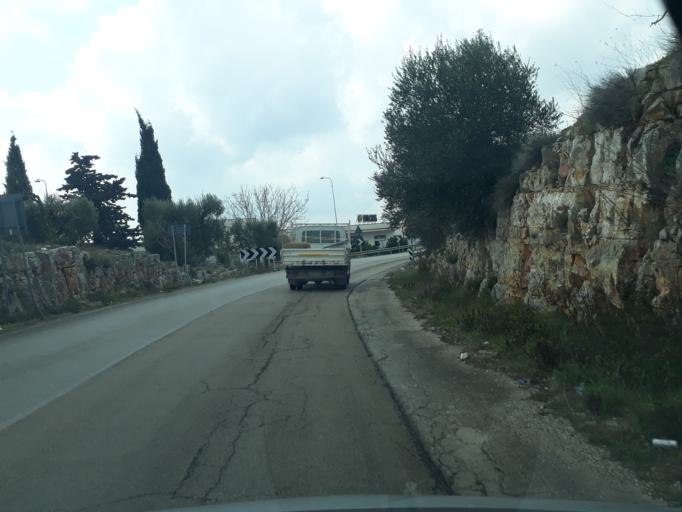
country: IT
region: Apulia
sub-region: Provincia di Brindisi
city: Cisternino
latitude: 40.7449
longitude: 17.4040
